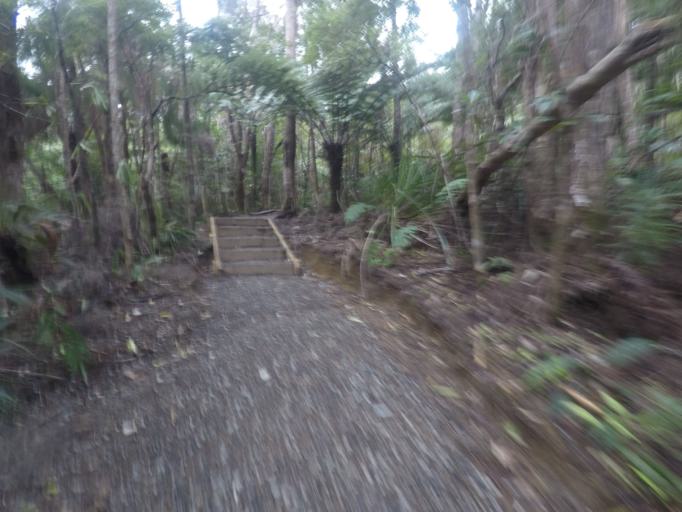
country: NZ
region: Auckland
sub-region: Auckland
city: Titirangi
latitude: -37.0019
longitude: 174.5377
